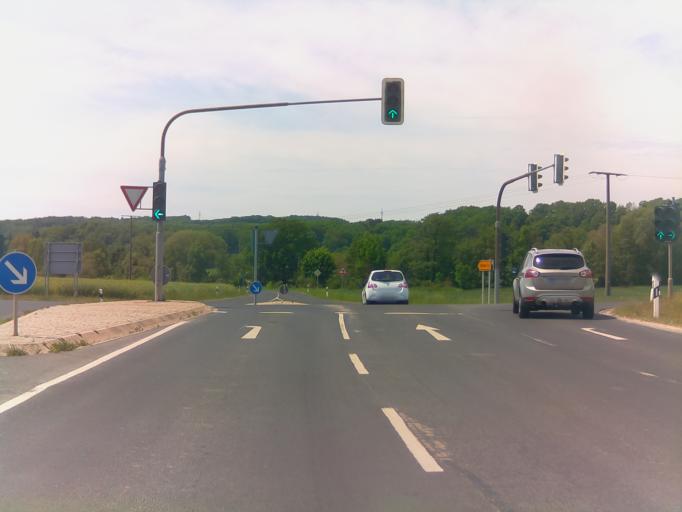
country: DE
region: Bavaria
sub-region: Regierungsbezirk Unterfranken
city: Salz
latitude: 50.3064
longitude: 10.1976
